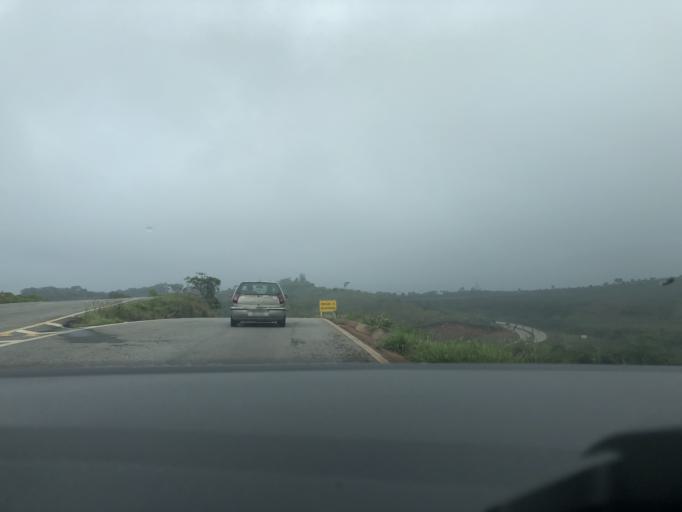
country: BR
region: Minas Gerais
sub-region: Congonhas
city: Congonhas
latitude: -20.5869
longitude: -43.9455
